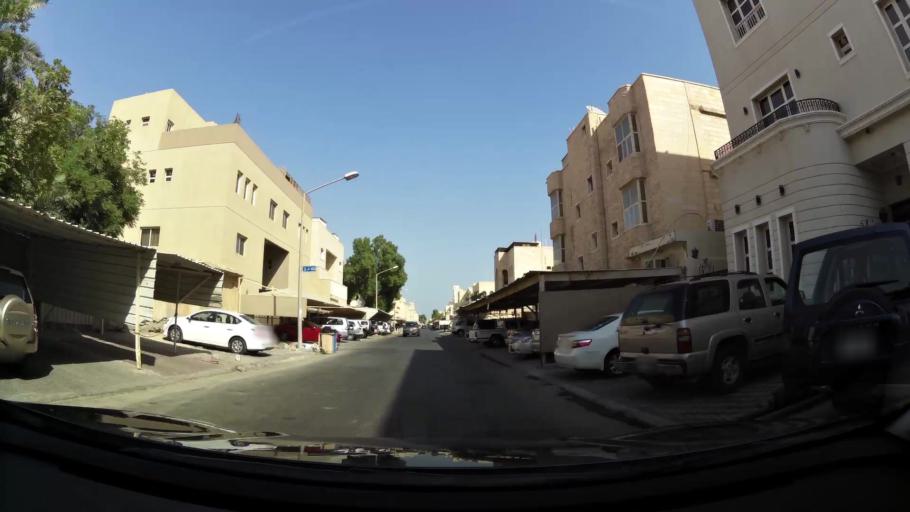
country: KW
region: Muhafazat Hawalli
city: Salwa
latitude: 29.2883
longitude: 48.0763
